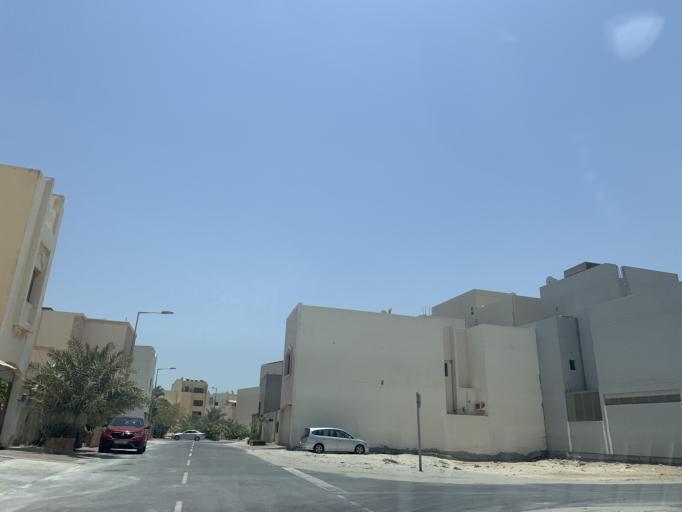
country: BH
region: Muharraq
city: Al Muharraq
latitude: 26.2861
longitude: 50.6185
